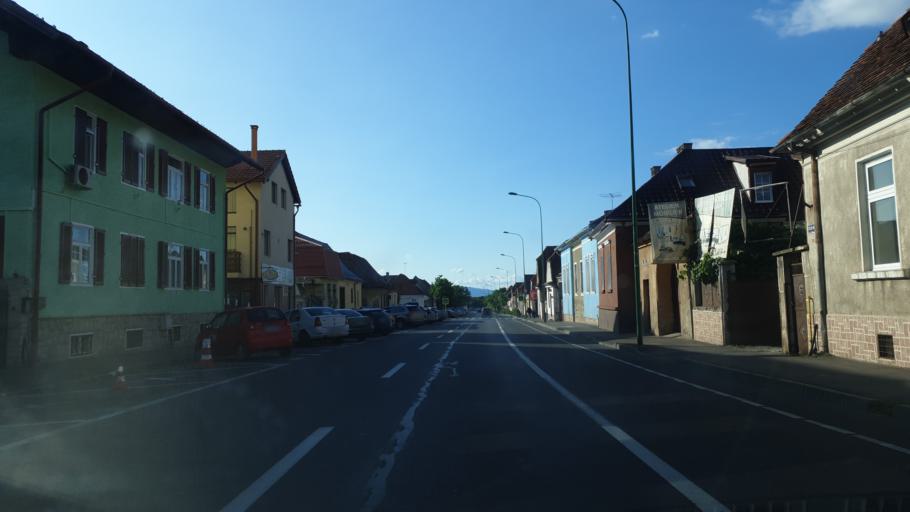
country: RO
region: Brasov
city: Brasov
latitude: 45.6565
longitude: 25.5850
